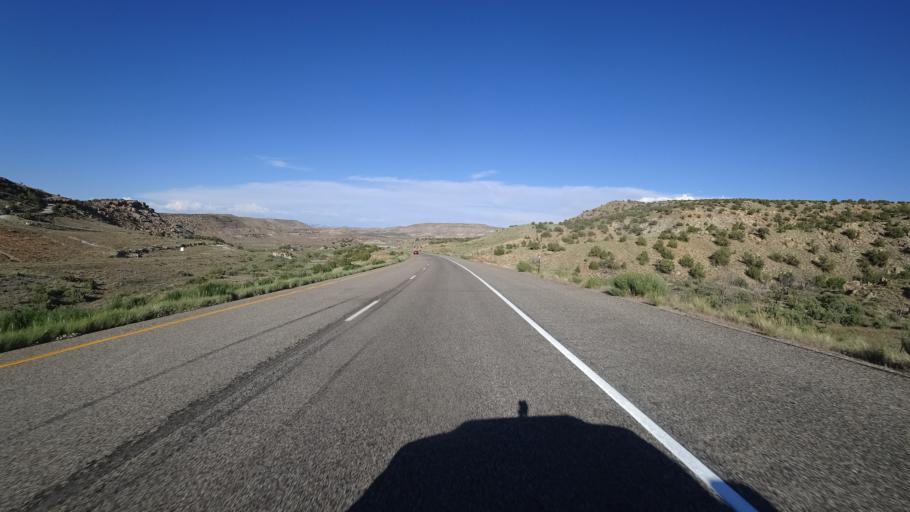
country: US
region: Colorado
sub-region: Mesa County
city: Loma
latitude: 39.1874
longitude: -109.0328
